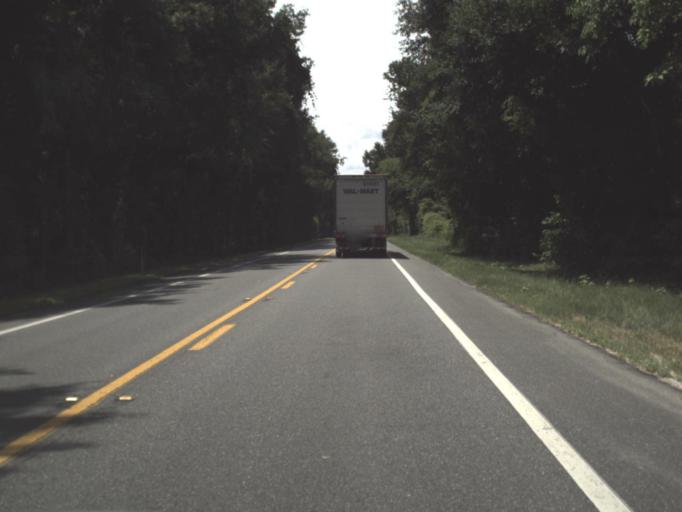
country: US
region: Florida
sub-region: Alachua County
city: Archer
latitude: 29.5865
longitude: -82.5568
